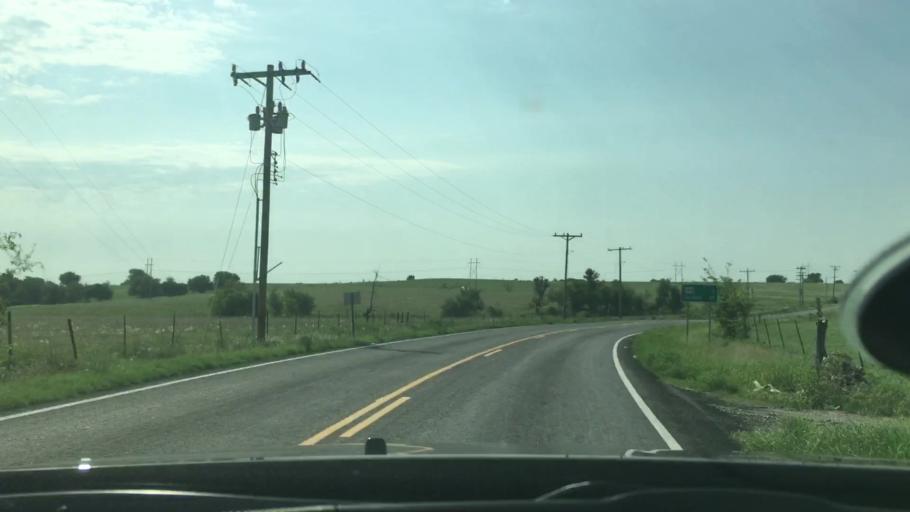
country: US
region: Oklahoma
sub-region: Bryan County
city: Durant
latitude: 34.1423
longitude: -96.4975
